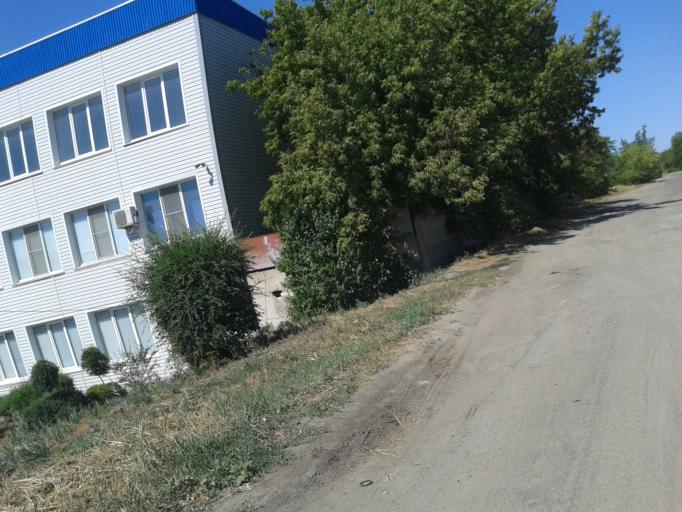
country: RU
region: Volgograd
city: Volgograd
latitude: 48.6917
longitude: 44.4430
